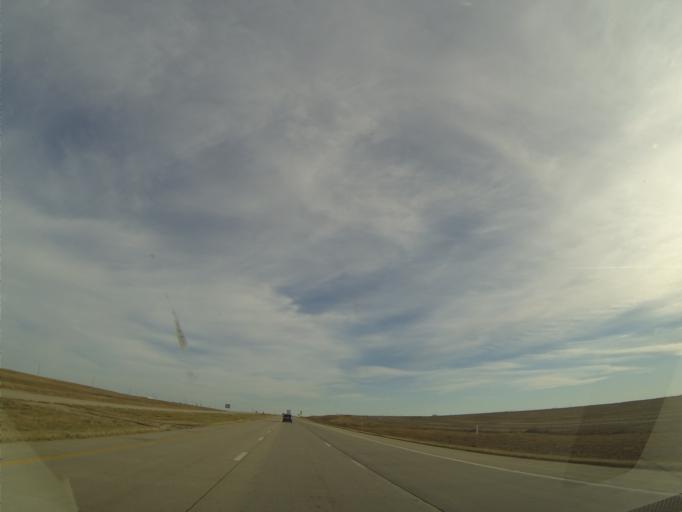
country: US
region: Kansas
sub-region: Ottawa County
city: Minneapolis
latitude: 39.1125
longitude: -97.6620
